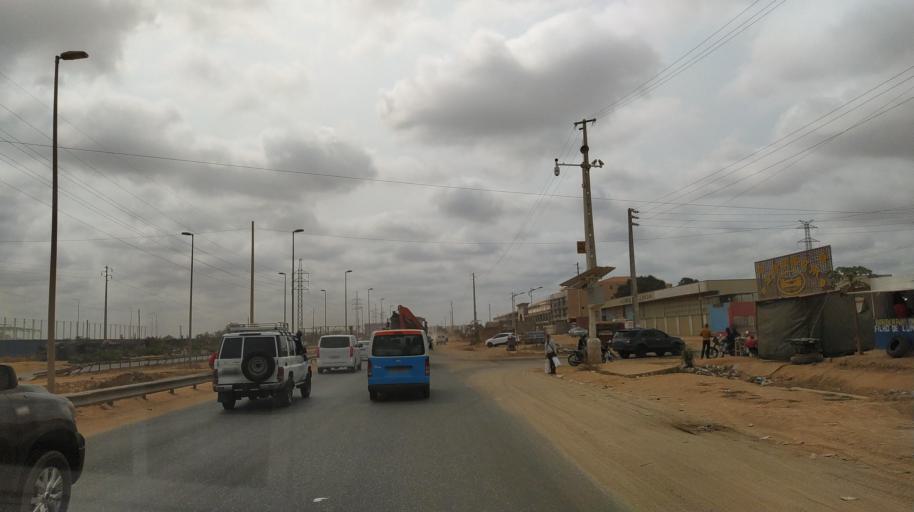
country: AO
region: Luanda
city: Luanda
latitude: -8.9777
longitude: 13.3758
